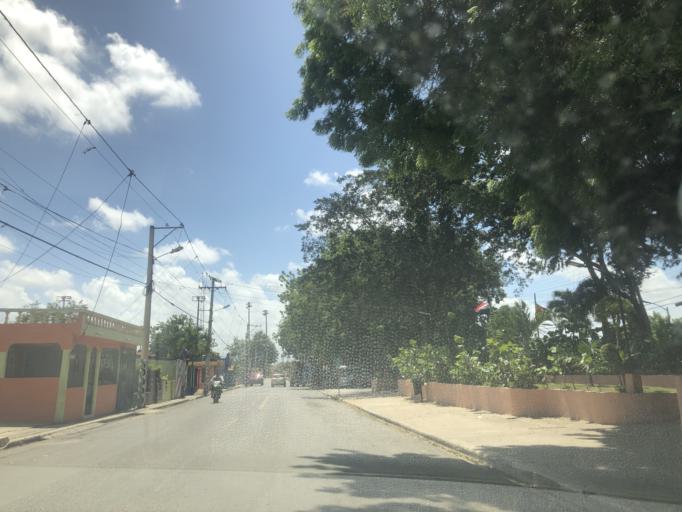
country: DO
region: Santiago
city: La Canela
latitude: 19.4510
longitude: -70.7798
